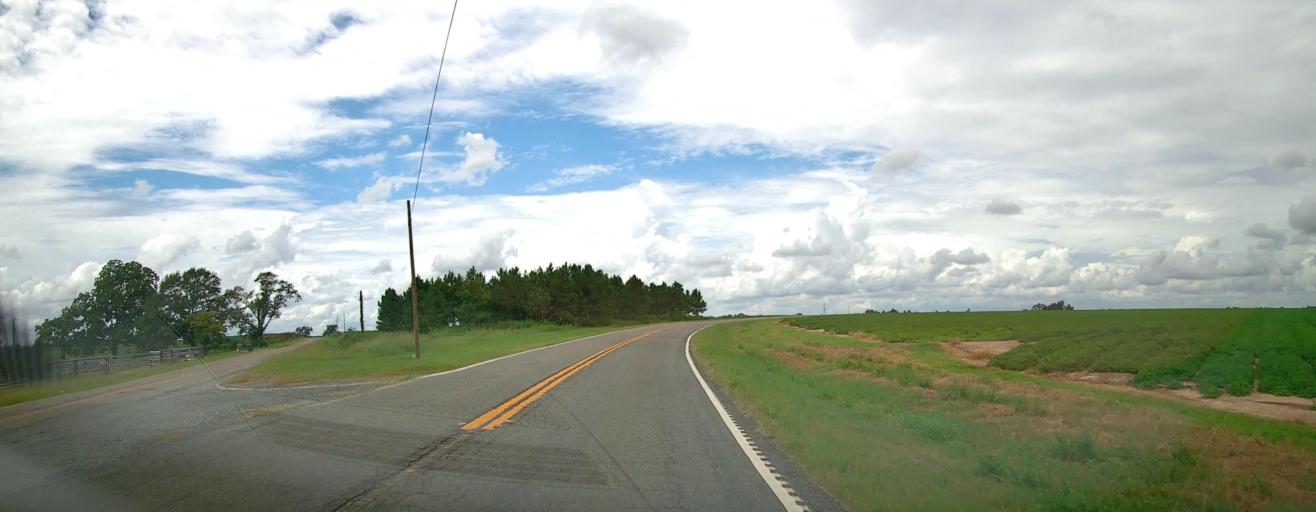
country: US
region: Georgia
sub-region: Dooly County
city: Unadilla
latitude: 32.2634
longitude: -83.8098
